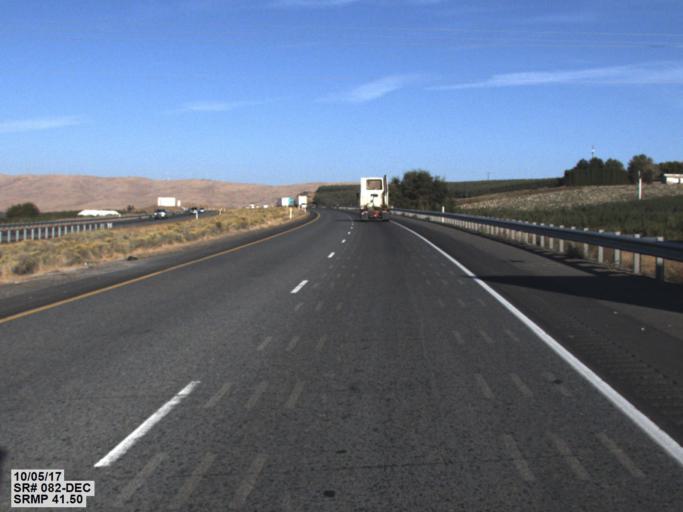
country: US
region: Washington
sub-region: Yakima County
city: Wapato
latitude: 46.4977
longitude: -120.4395
